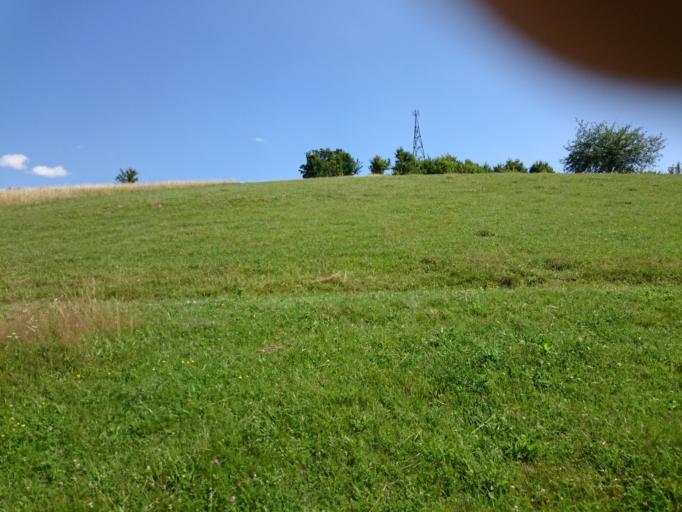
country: RO
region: Mures
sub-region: Municipiul Sighisoara
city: Sighisoara
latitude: 46.2141
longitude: 24.7988
